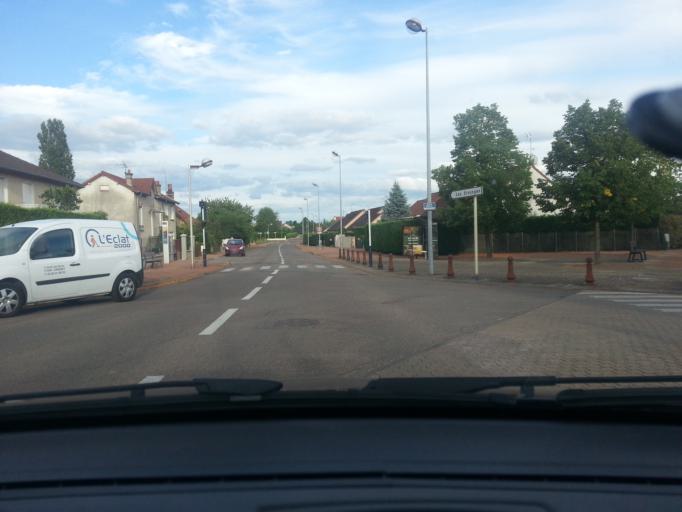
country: FR
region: Bourgogne
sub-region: Departement de Saone-et-Loire
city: Chatenoy-le-Royal
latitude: 46.8014
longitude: 4.8135
